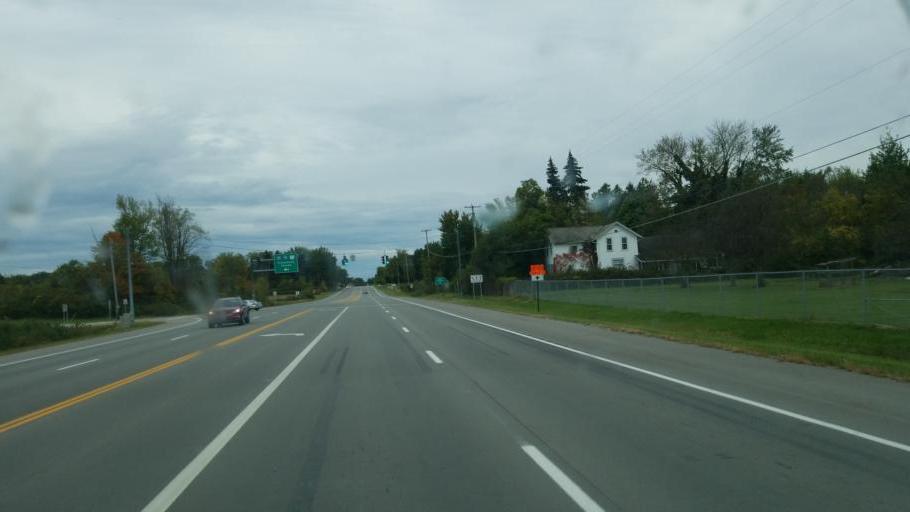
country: US
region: Ohio
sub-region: Lorain County
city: Amherst
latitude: 41.3775
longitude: -82.2104
